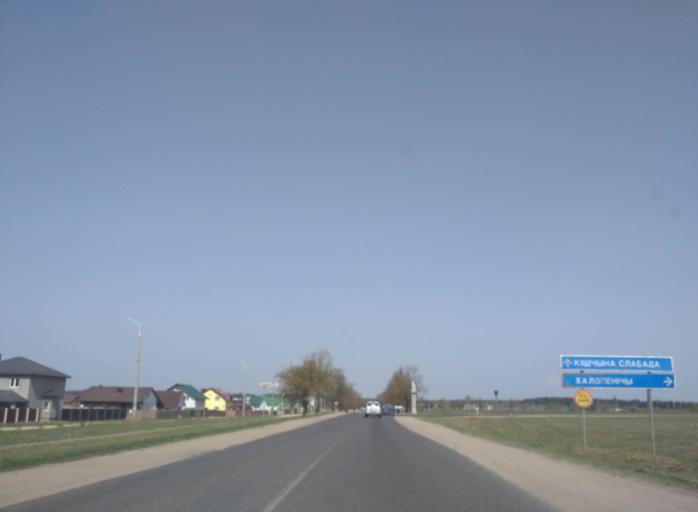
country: BY
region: Minsk
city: Horad Barysaw
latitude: 54.2732
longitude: 28.4969
